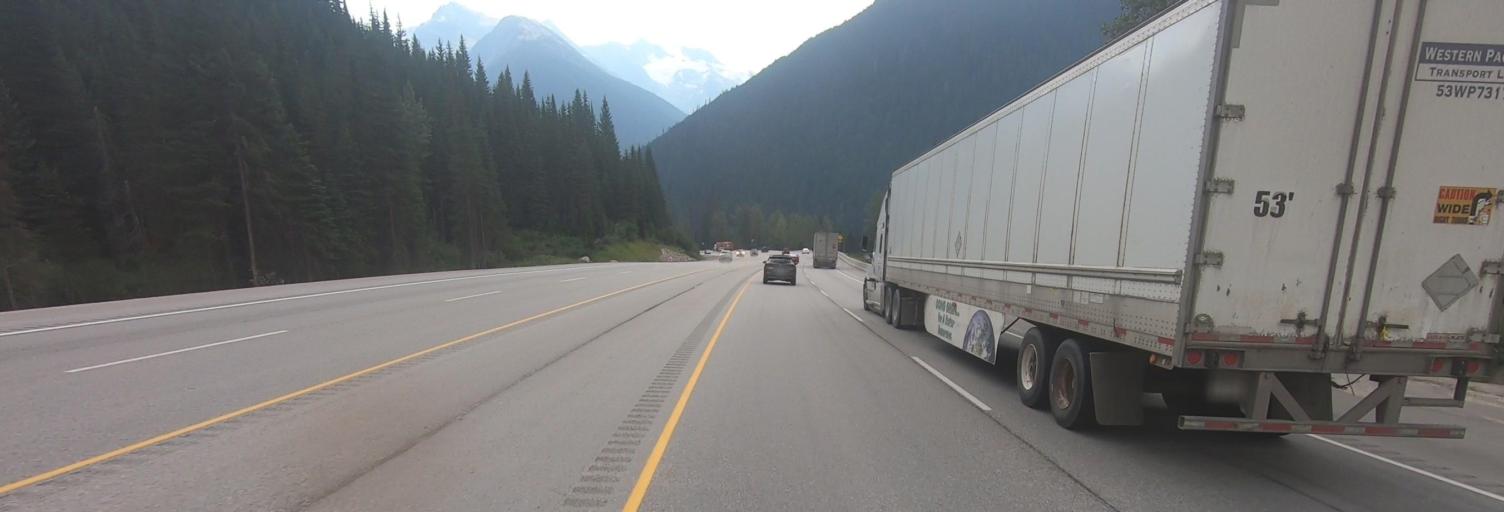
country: CA
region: British Columbia
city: Golden
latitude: 51.2761
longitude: -117.5095
